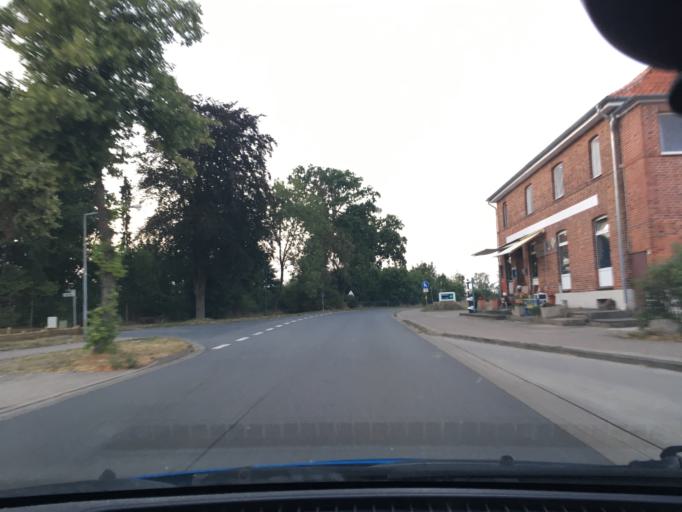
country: DE
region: Lower Saxony
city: Embsen
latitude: 53.1772
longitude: 10.3453
